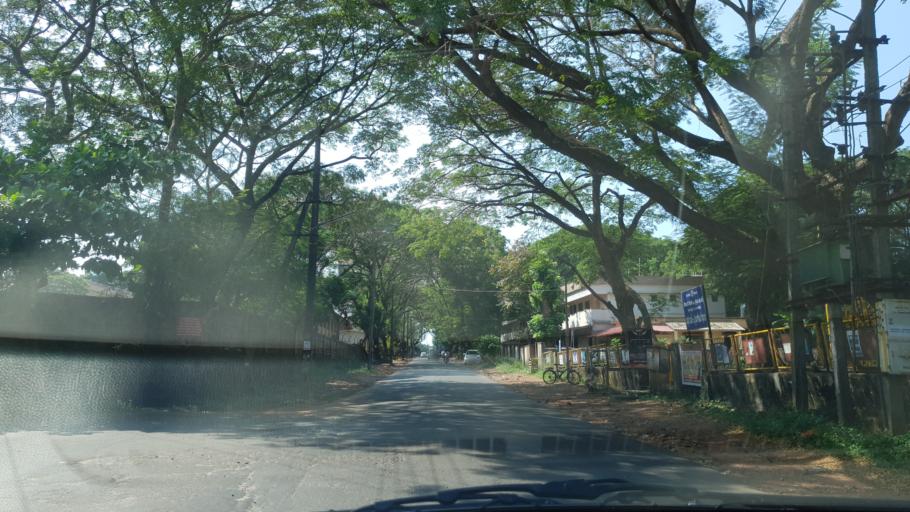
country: IN
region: Karnataka
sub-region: Dakshina Kannada
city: Mangalore
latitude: 12.8845
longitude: 74.8363
